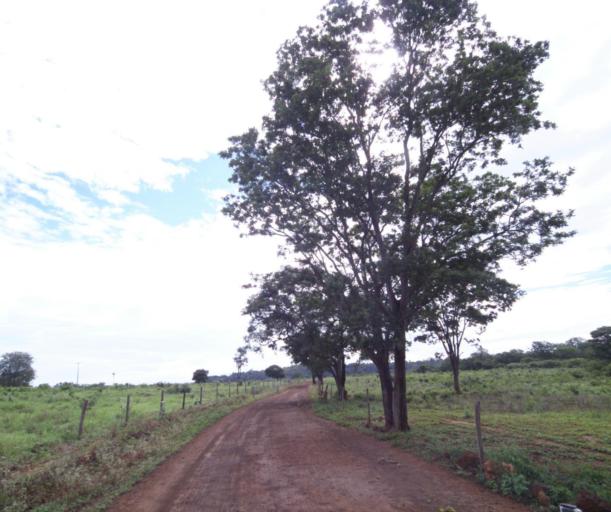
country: BR
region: Bahia
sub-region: Carinhanha
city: Carinhanha
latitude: -14.2463
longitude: -44.4222
